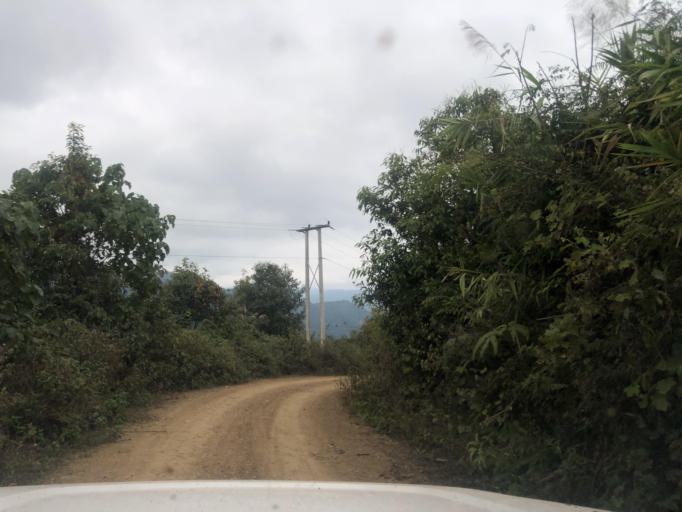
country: LA
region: Phongsali
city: Khoa
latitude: 21.2588
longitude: 102.5901
